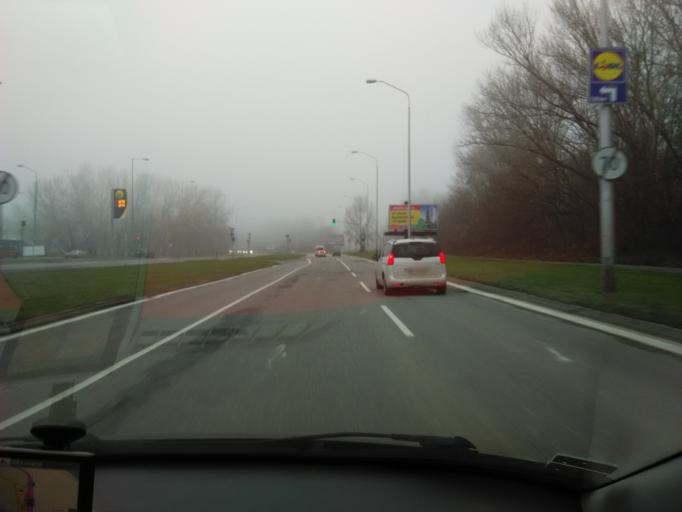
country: SK
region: Bratislavsky
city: Bratislava
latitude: 48.1159
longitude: 17.1330
